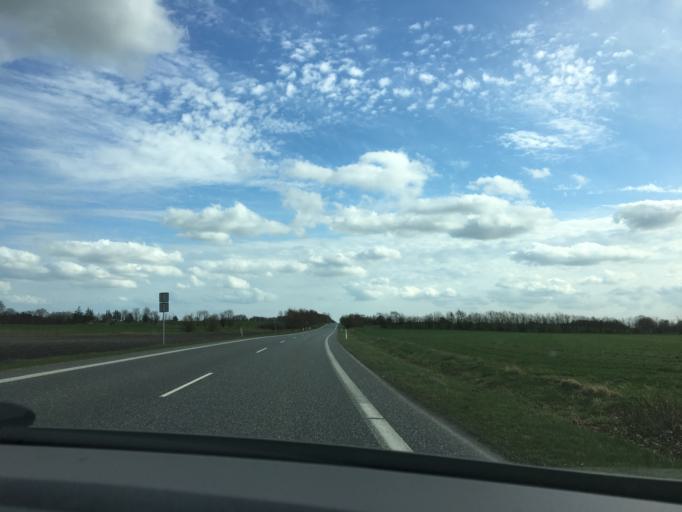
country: DK
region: South Denmark
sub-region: Vejle Kommune
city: Jelling
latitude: 55.7977
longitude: 9.3778
